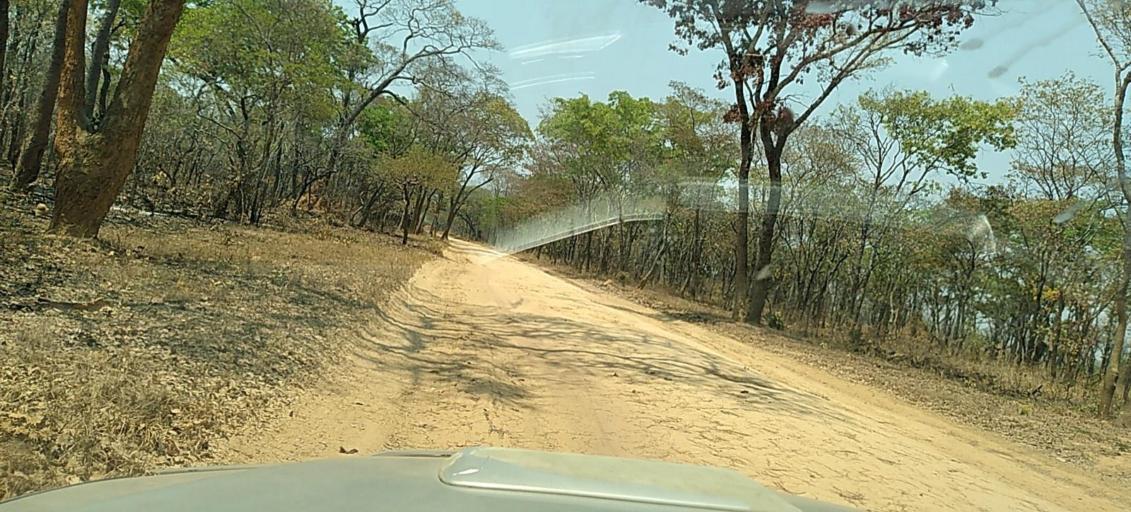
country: ZM
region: North-Western
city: Kasempa
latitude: -13.6090
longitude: 26.1892
